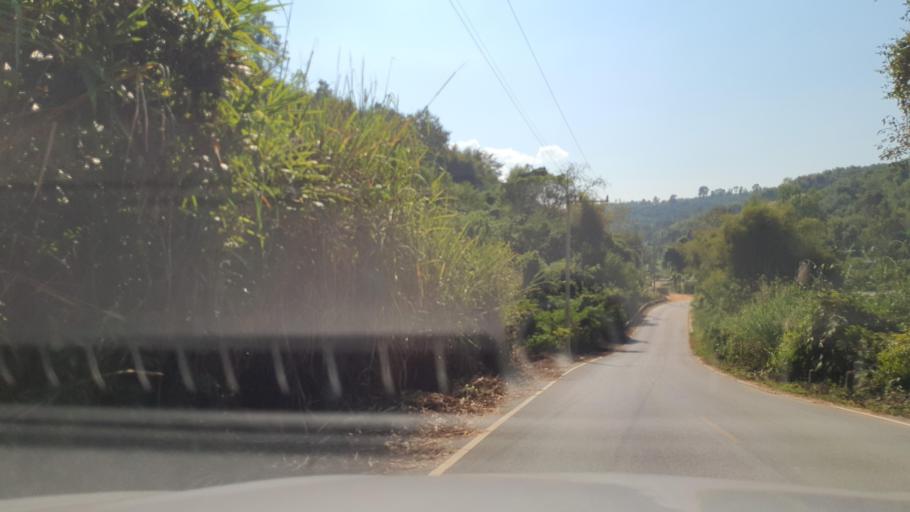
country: TH
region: Nan
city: Pua
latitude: 19.1658
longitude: 100.9097
